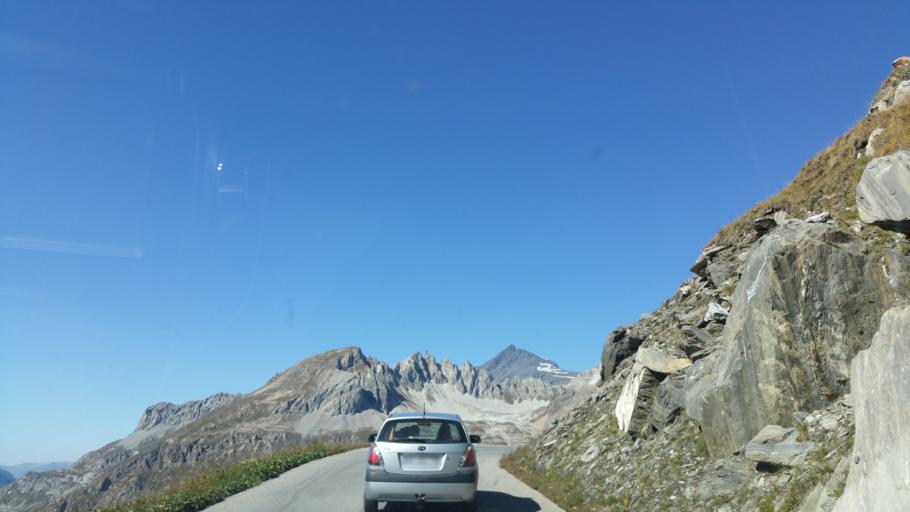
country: FR
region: Rhone-Alpes
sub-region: Departement de la Savoie
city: Val-d'Isere
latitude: 45.4331
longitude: 7.0033
